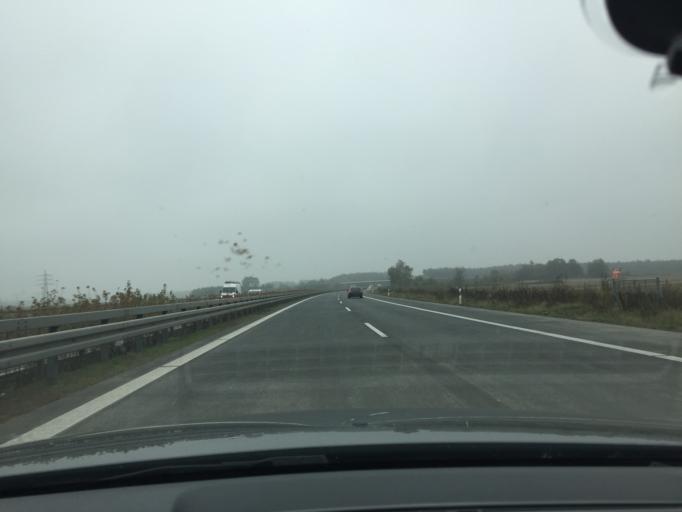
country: DE
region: Brandenburg
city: Lubbenau
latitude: 51.8734
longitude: 13.8934
